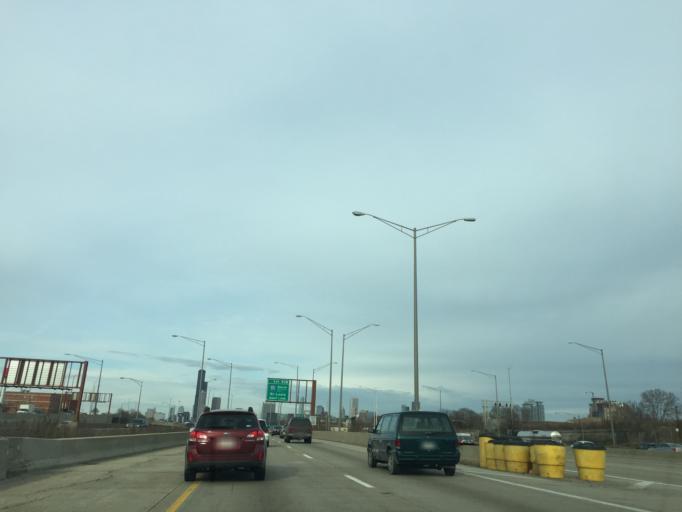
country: US
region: Illinois
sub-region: Cook County
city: Chicago
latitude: 41.8401
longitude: -87.6308
